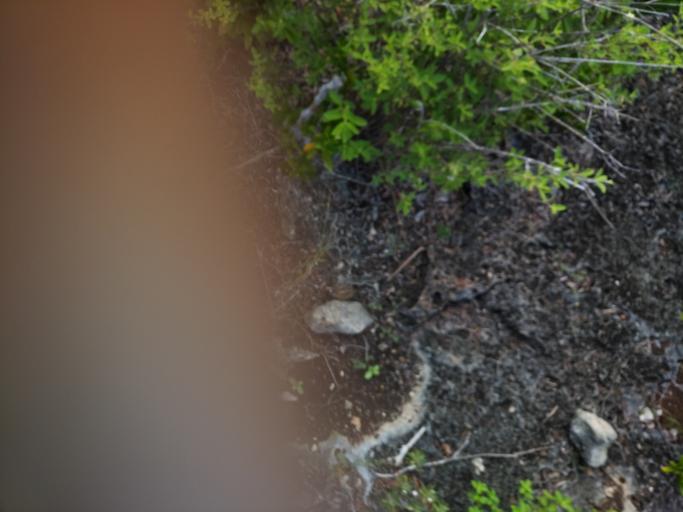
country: AI
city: Island Harbour
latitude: 18.2601
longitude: -63.0087
